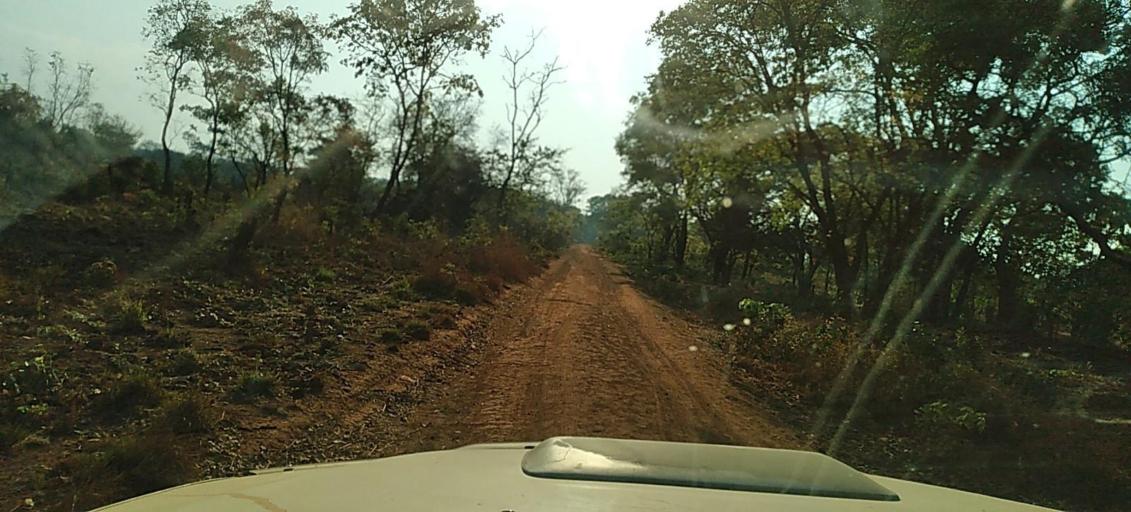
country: ZM
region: North-Western
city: Kasempa
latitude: -13.1674
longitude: 25.8840
